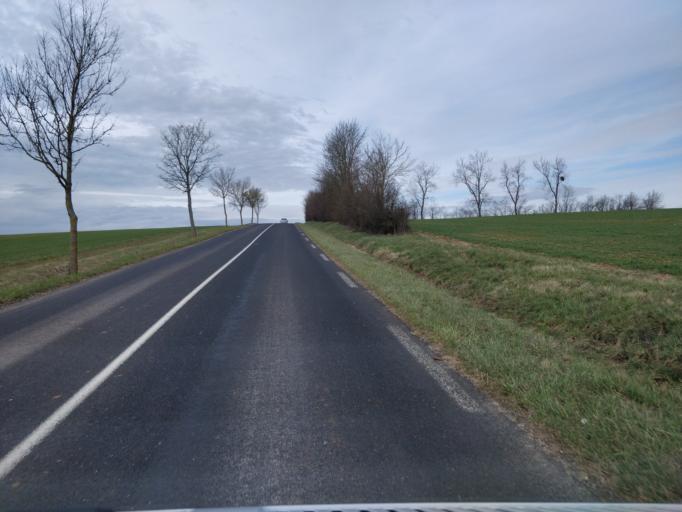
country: FR
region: Lorraine
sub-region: Departement de Meurthe-et-Moselle
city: Montauville
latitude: 48.9054
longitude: 5.9469
